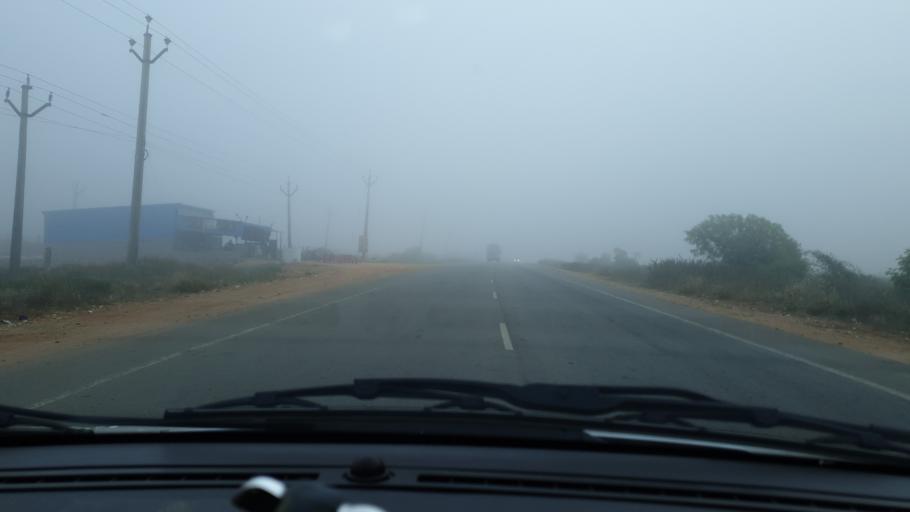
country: IN
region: Telangana
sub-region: Mahbubnagar
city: Nagar Karnul
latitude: 16.6627
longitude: 78.5375
